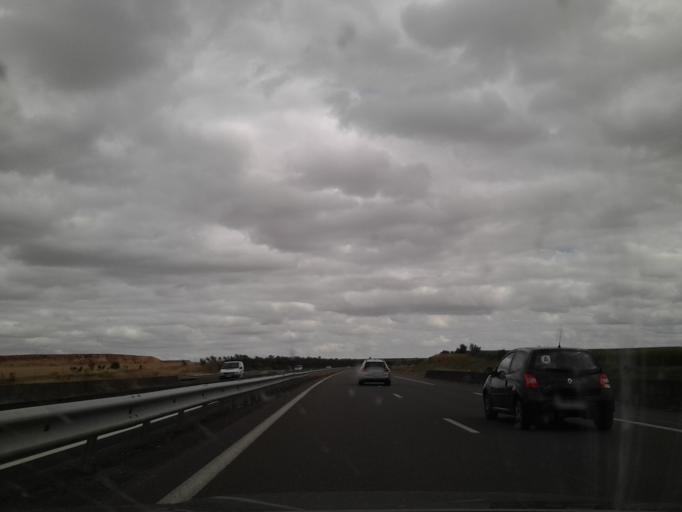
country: FR
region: Centre
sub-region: Departement du Cher
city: Trouy
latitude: 47.0061
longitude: 2.3946
